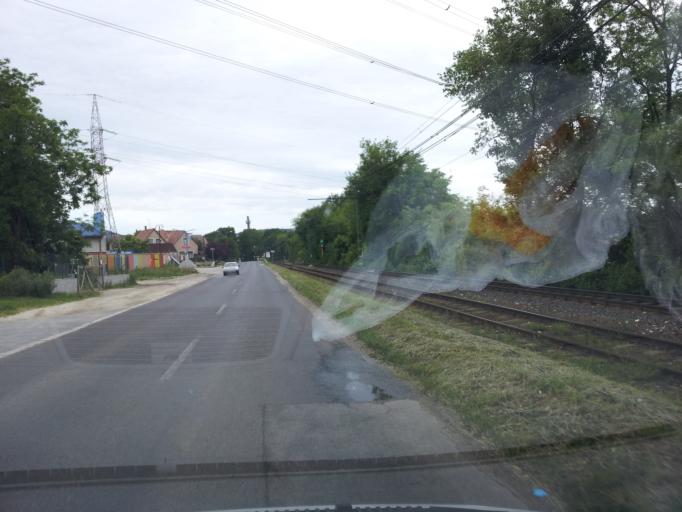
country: HU
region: Pest
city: Pomaz
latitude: 47.6370
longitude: 19.0392
